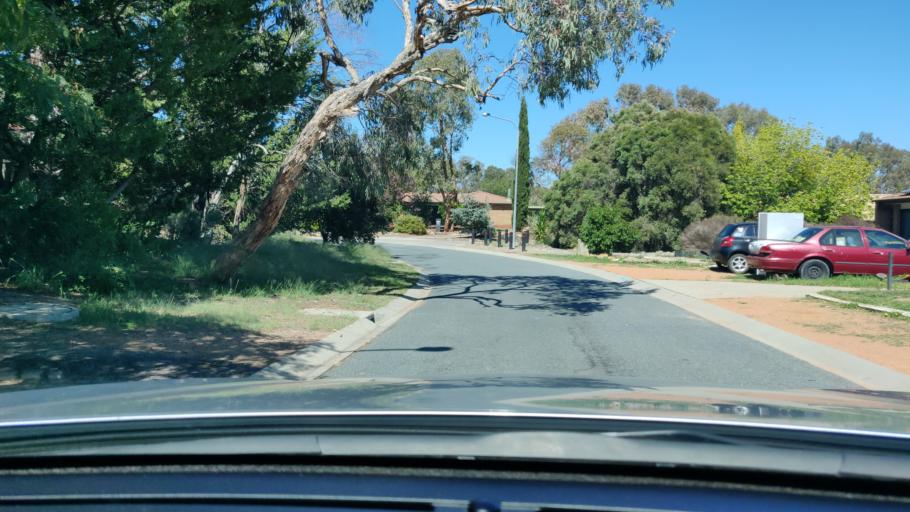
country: AU
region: Australian Capital Territory
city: Macarthur
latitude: -35.4419
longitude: 149.0971
